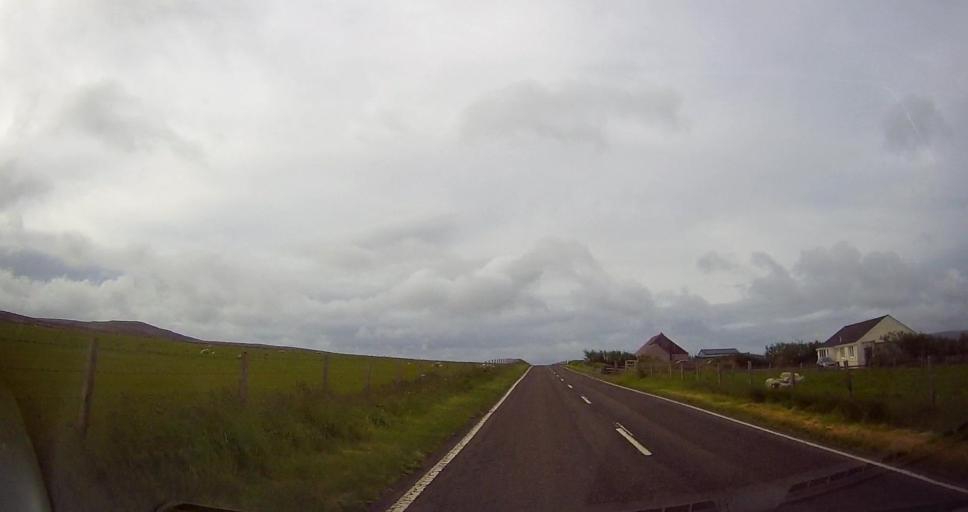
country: GB
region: Scotland
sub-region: Orkney Islands
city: Stromness
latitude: 58.9544
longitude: -3.2190
